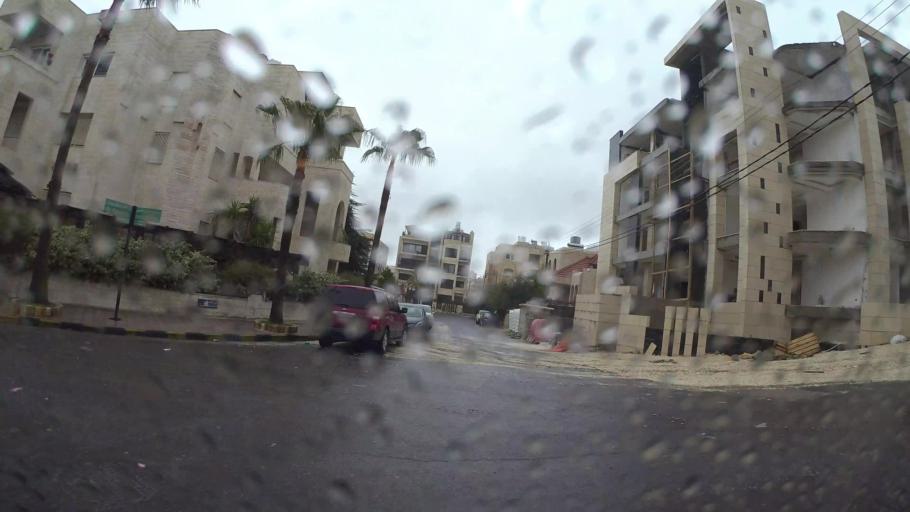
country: JO
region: Amman
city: Wadi as Sir
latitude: 31.9716
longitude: 35.8486
